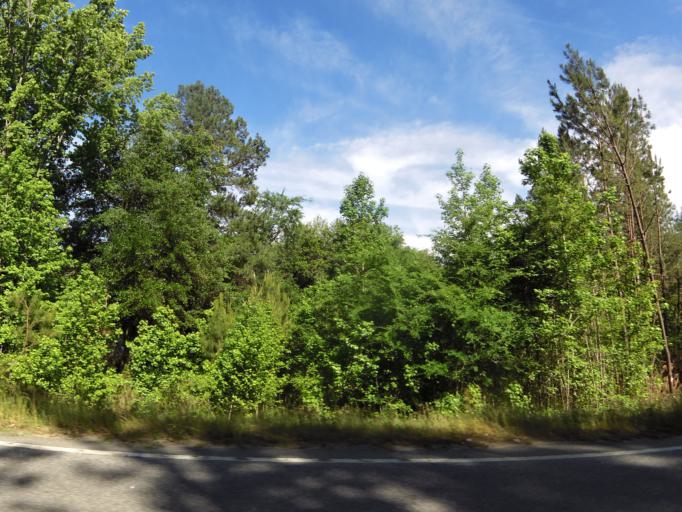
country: US
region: South Carolina
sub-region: Bamberg County
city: Denmark
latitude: 33.2878
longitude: -81.1486
